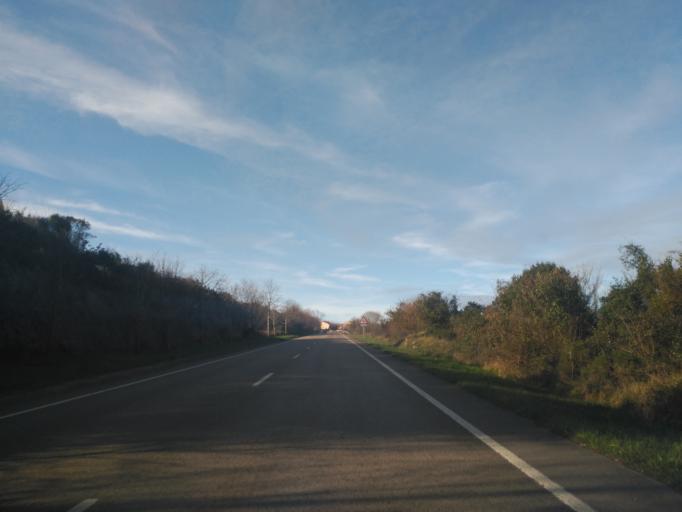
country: ES
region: Cantabria
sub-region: Provincia de Cantabria
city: Comillas
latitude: 43.3487
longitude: -4.2656
